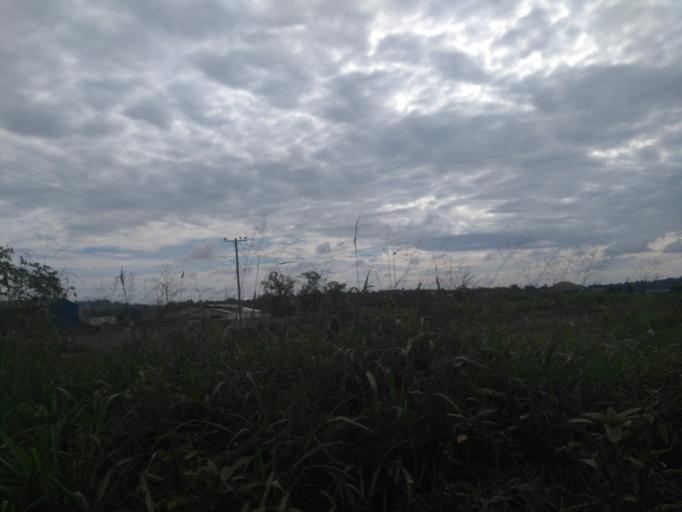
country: UG
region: Eastern Region
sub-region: Jinja District
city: Jinja
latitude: 0.4342
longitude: 33.1850
